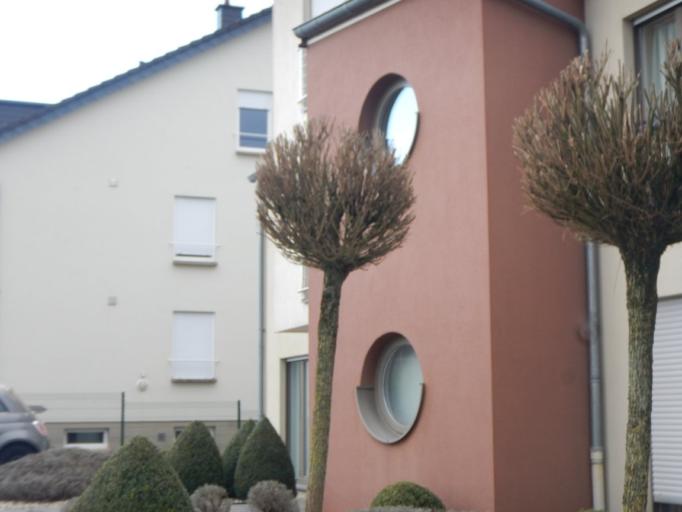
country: LU
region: Diekirch
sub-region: Canton de Redange
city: Ell
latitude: 49.7637
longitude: 5.8222
